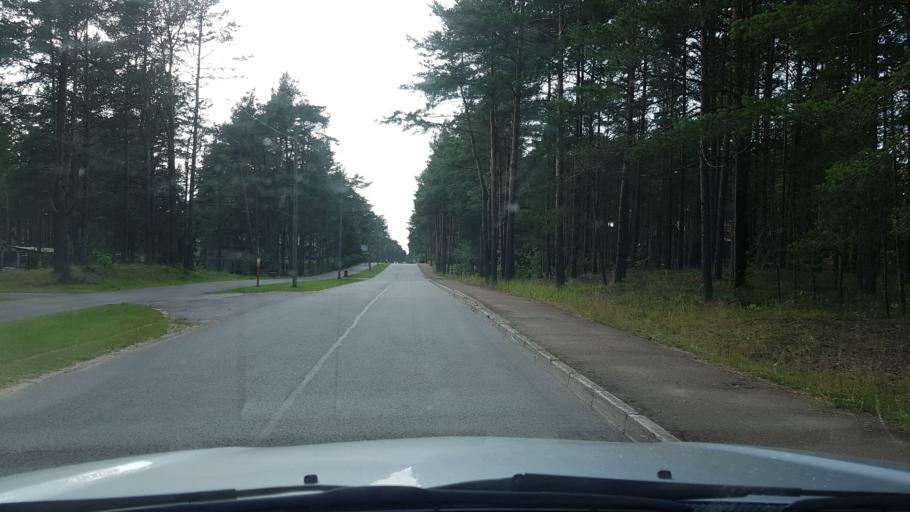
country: EE
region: Ida-Virumaa
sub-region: Narva-Joesuu linn
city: Narva-Joesuu
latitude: 59.4522
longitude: 28.0568
